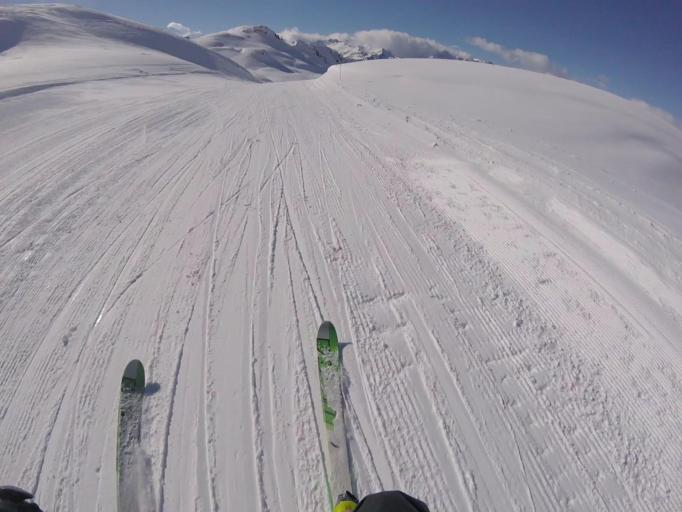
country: ES
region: Catalonia
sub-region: Provincia de Lleida
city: Vielha
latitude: 42.7279
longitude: 0.9397
